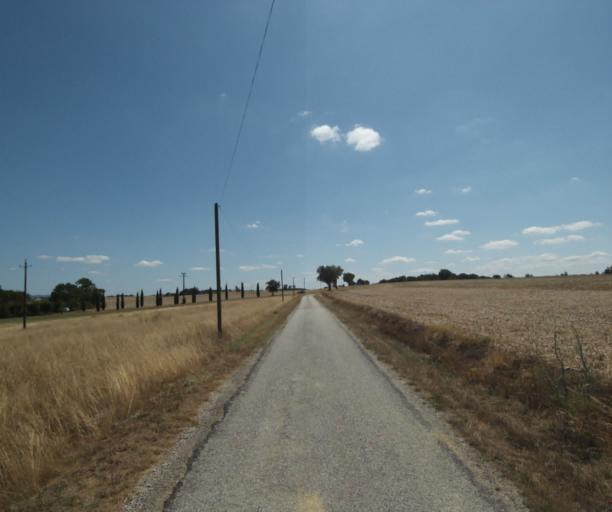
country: FR
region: Midi-Pyrenees
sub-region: Departement de la Haute-Garonne
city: Auriac-sur-Vendinelle
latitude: 43.4915
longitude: 1.8562
